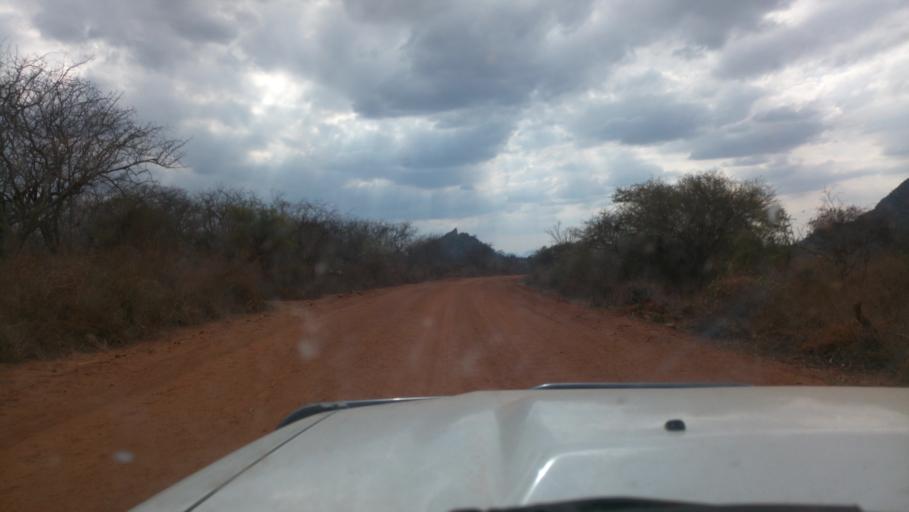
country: KE
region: Kitui
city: Kitui
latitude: -1.7563
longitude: 38.4245
